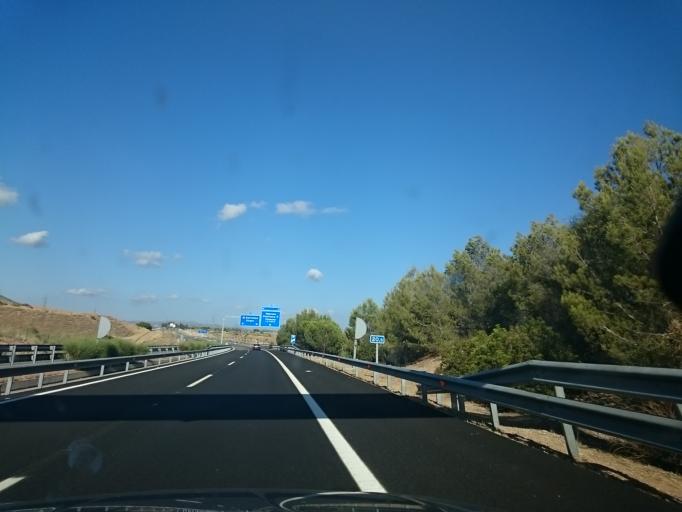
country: ES
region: Catalonia
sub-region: Provincia de Barcelona
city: Vilanova i la Geltru
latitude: 41.2496
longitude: 1.7063
